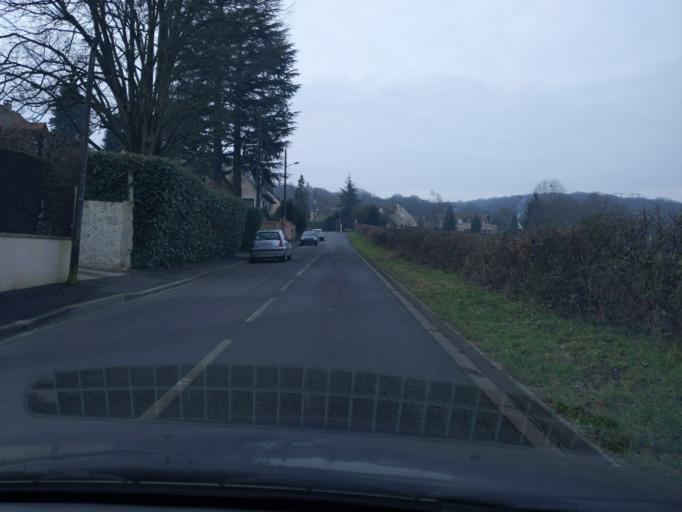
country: FR
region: Ile-de-France
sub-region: Departement des Yvelines
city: Saint-Remy-les-Chevreuse
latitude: 48.7166
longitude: 2.0639
